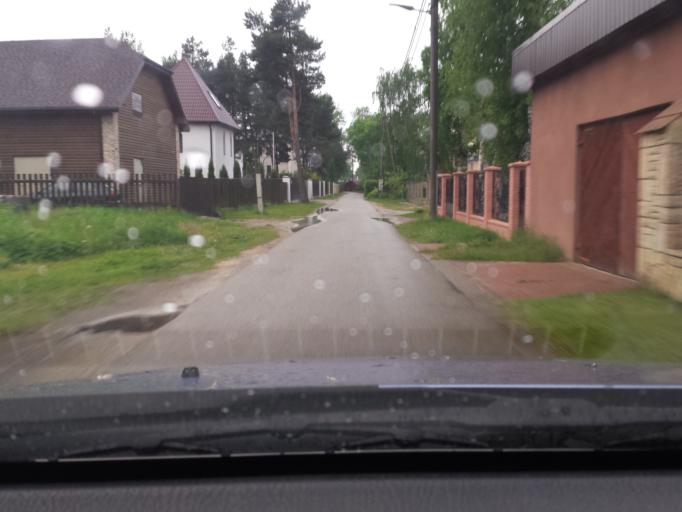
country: LV
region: Riga
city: Bolderaja
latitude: 57.0507
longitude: 24.1002
